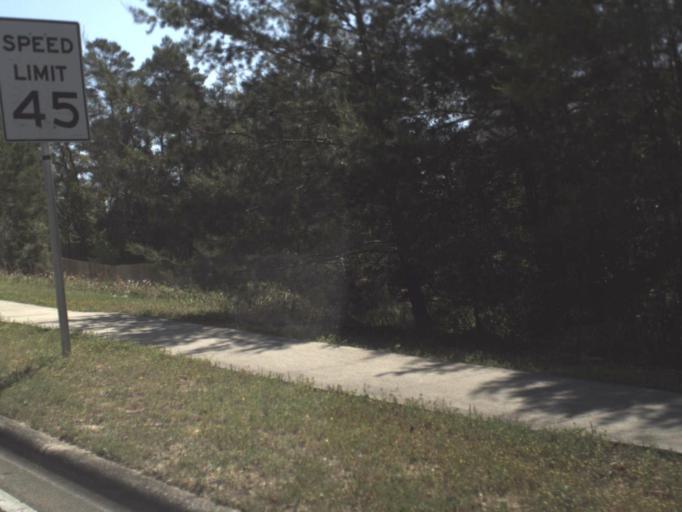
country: US
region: Florida
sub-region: Okaloosa County
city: Niceville
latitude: 30.5281
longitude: -86.4658
